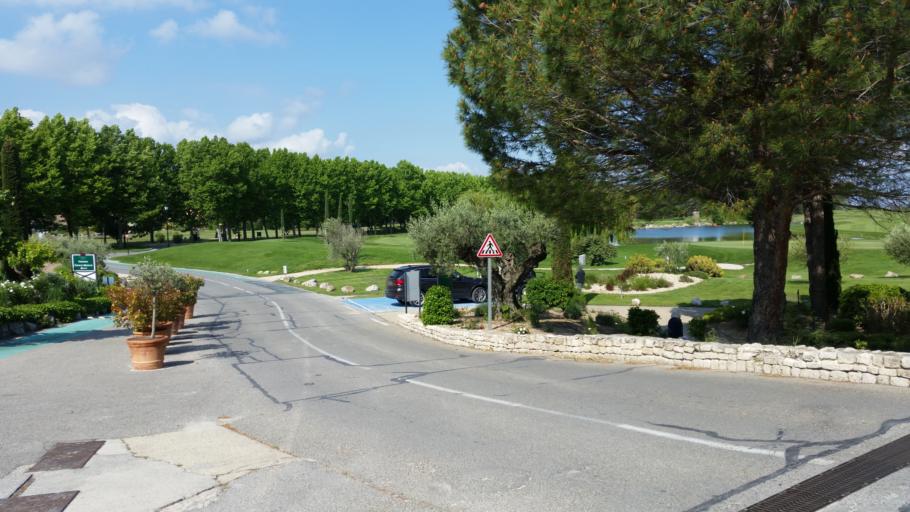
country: FR
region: Provence-Alpes-Cote d'Azur
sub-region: Departement des Bouches-du-Rhone
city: Charleval
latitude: 43.7073
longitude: 5.2097
